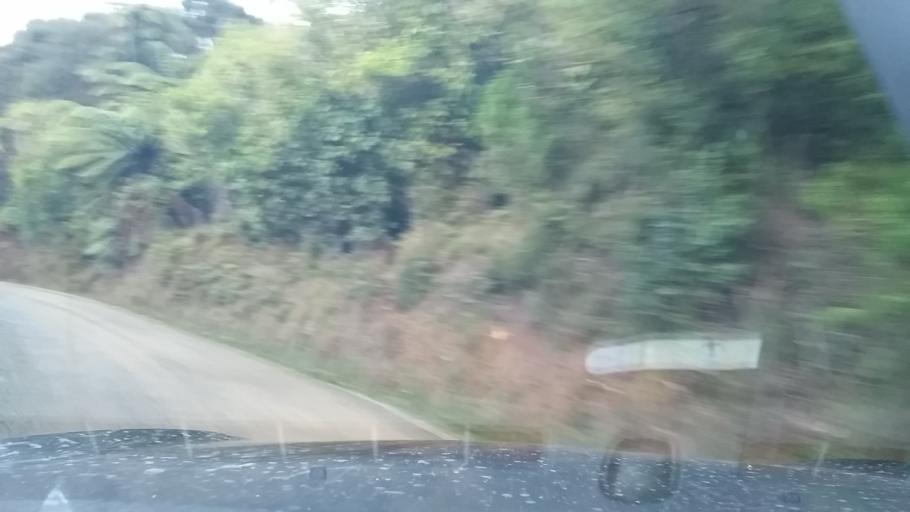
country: NZ
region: Marlborough
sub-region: Marlborough District
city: Picton
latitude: -41.1318
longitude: 174.1456
